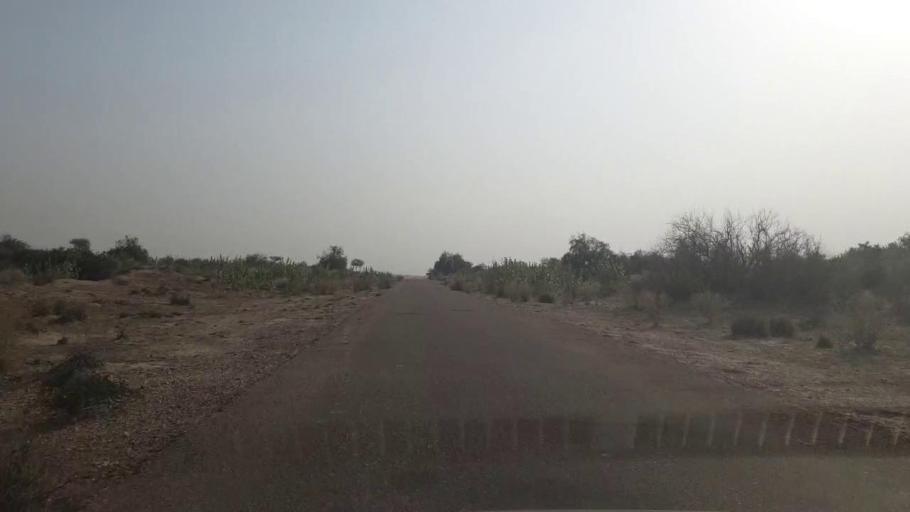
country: PK
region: Sindh
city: Chor
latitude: 25.4805
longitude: 69.9746
